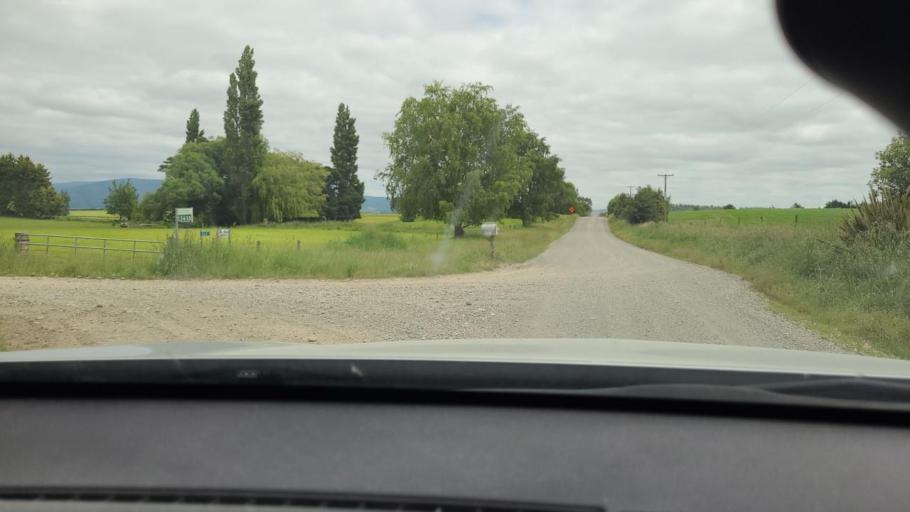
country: NZ
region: Southland
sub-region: Southland District
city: Riverton
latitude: -46.0658
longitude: 168.0277
